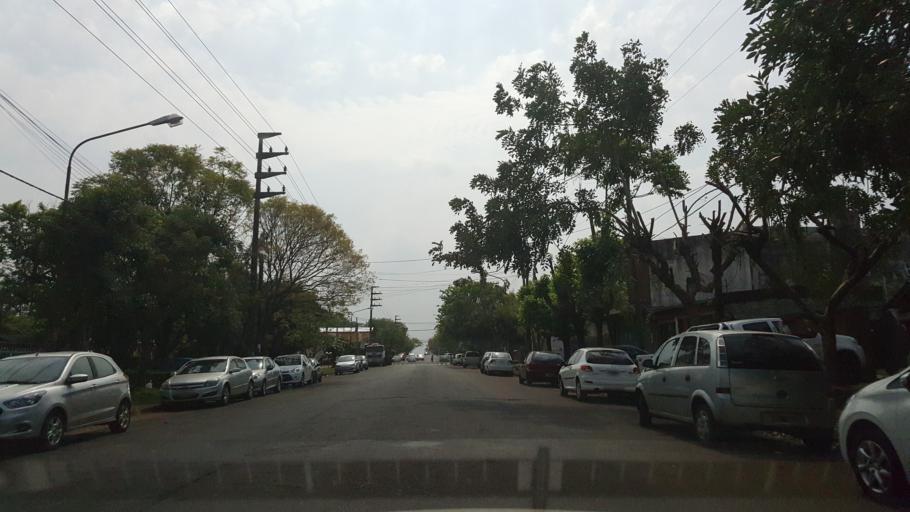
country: AR
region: Misiones
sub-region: Departamento de Capital
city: Posadas
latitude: -27.3643
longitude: -55.9086
